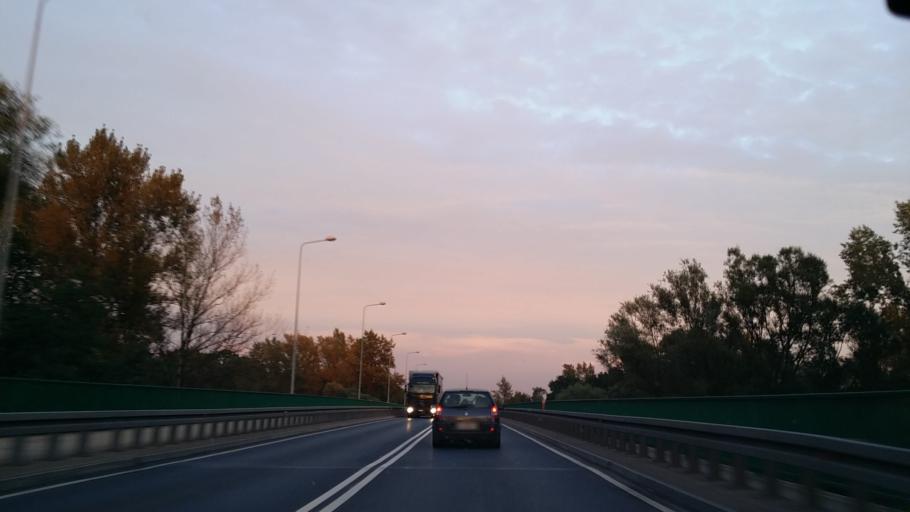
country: PL
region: Lesser Poland Voivodeship
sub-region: Powiat oswiecimski
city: Oswiecim
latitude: 50.0331
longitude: 19.2130
